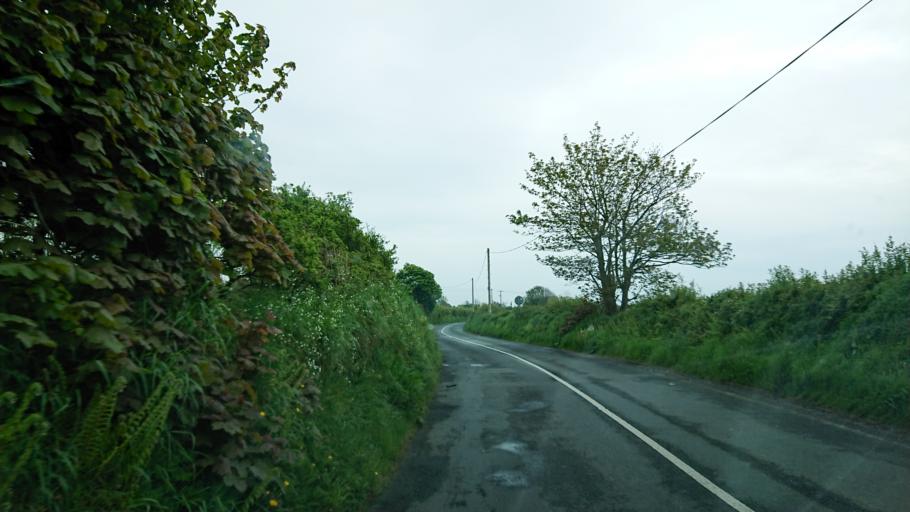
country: IE
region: Munster
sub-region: Waterford
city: Waterford
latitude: 52.2281
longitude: -7.0597
